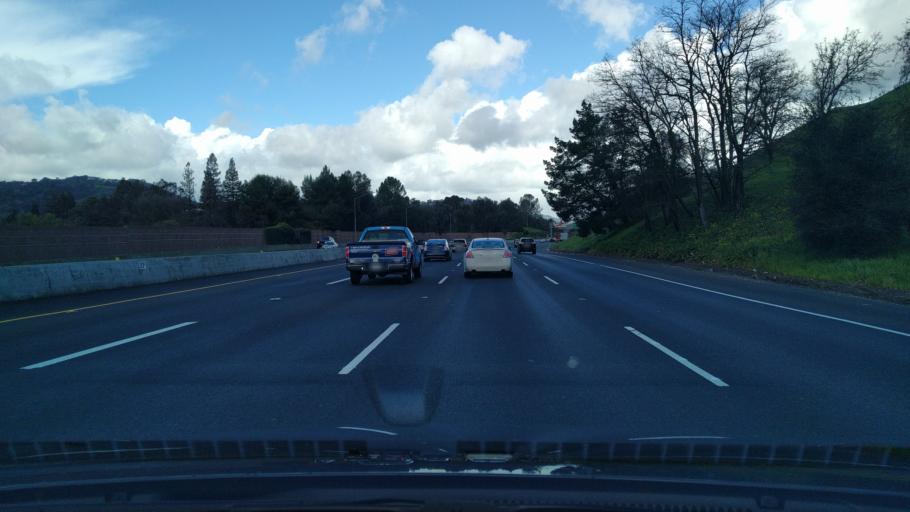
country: US
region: California
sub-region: Contra Costa County
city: Alamo
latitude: 37.8457
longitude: -122.0253
